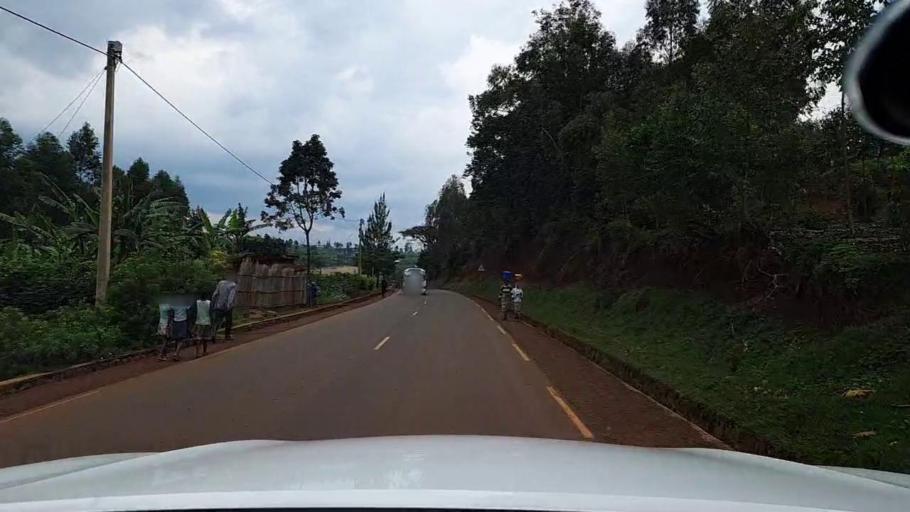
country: RW
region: Western Province
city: Cyangugu
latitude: -2.6126
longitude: 28.9390
